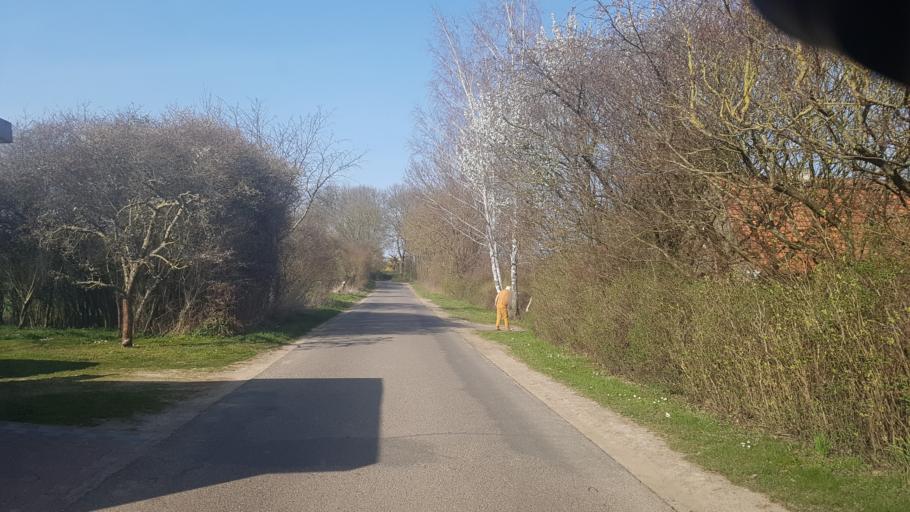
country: DE
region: Brandenburg
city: Gerswalde
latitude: 53.2043
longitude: 13.7825
